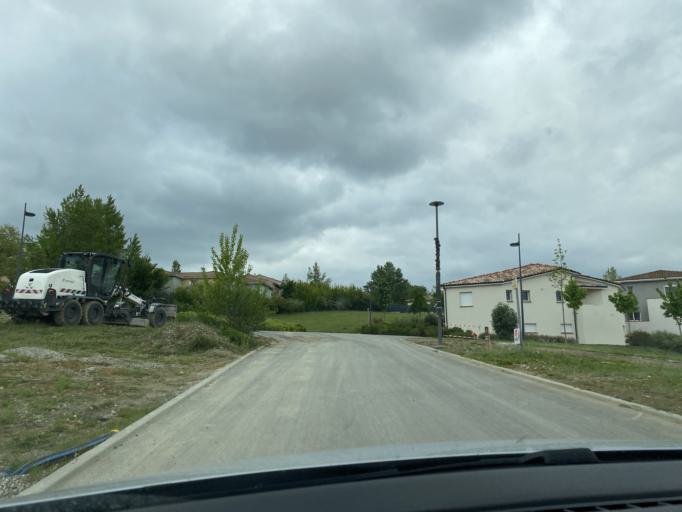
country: FR
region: Midi-Pyrenees
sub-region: Departement de la Haute-Garonne
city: Nailloux
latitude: 43.3618
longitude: 1.6227
